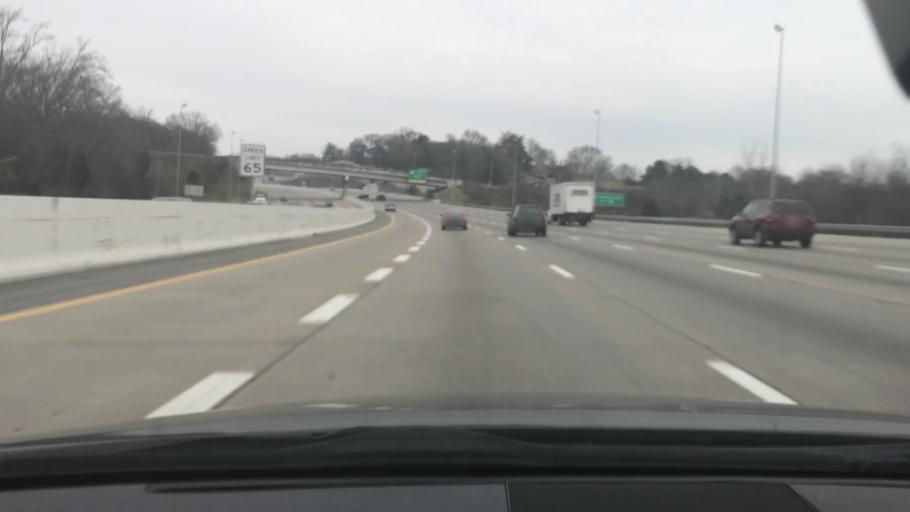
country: US
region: Tennessee
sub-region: Davidson County
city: Goodlettsville
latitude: 36.2529
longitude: -86.7394
